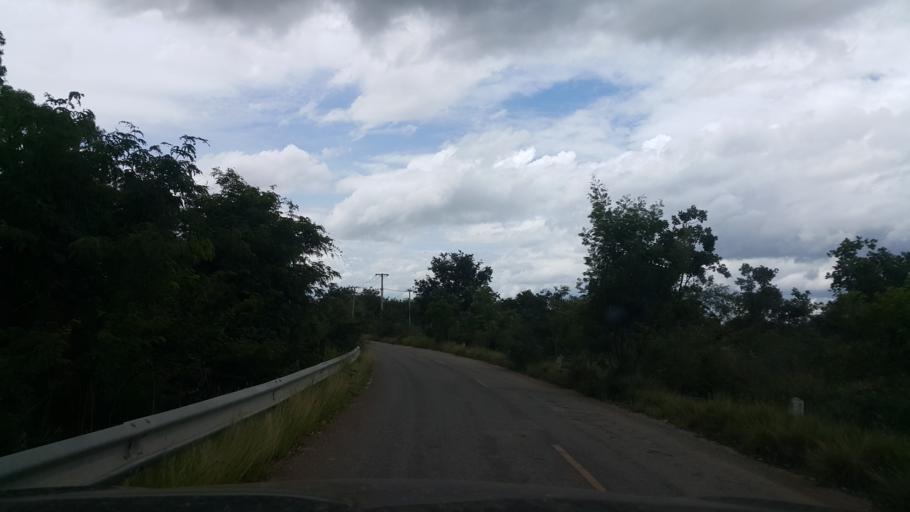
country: TH
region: Sukhothai
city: Ban Na
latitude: 17.0491
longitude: 99.7759
